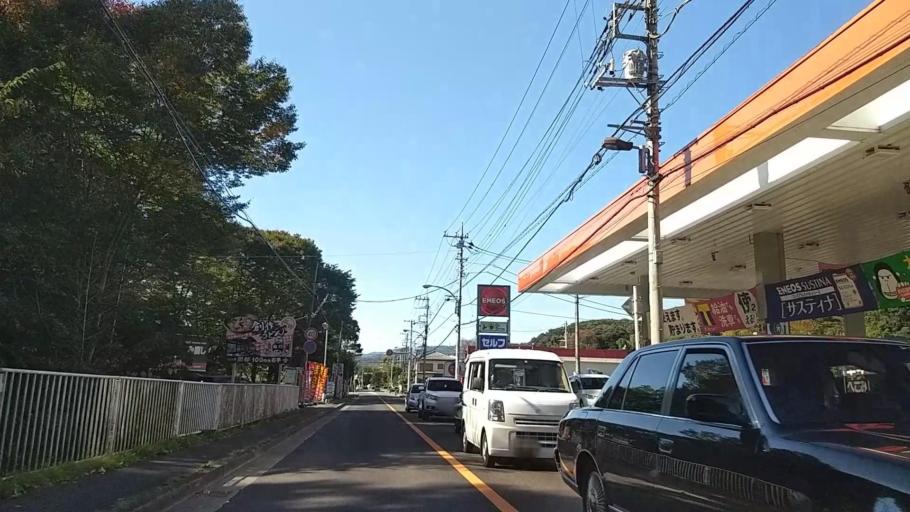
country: JP
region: Tokyo
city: Hachioji
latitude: 35.6061
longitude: 139.3182
